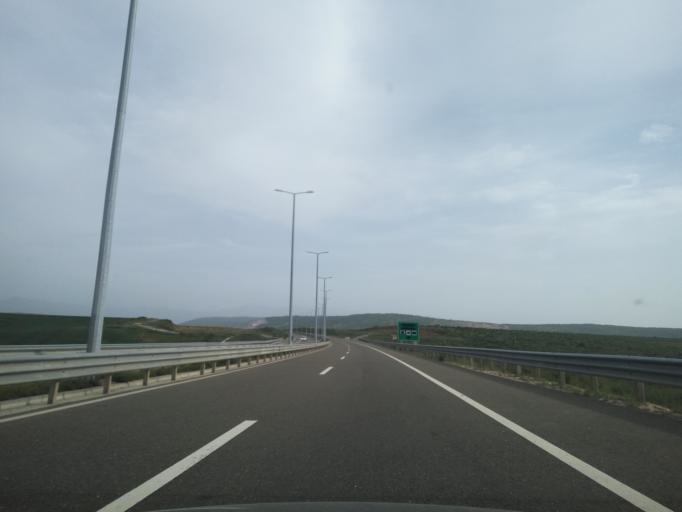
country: XK
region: Prizren
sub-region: Komuna e Malisheves
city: Malisevo
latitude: 42.4848
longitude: 20.7935
